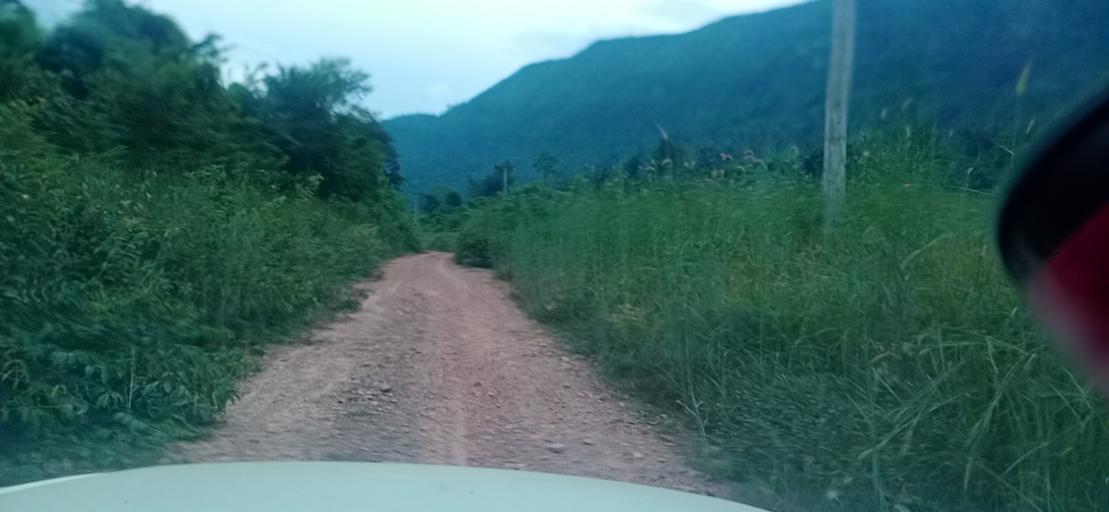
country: TH
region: Changwat Bueng Kan
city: Pak Khat
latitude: 18.5631
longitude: 103.2839
